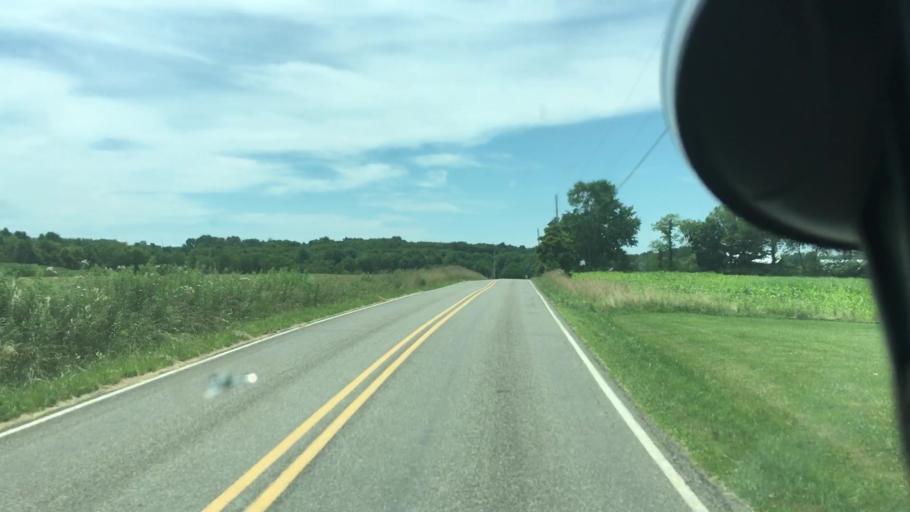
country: US
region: Pennsylvania
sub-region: Mercer County
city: Mercer
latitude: 41.2279
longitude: -80.1974
